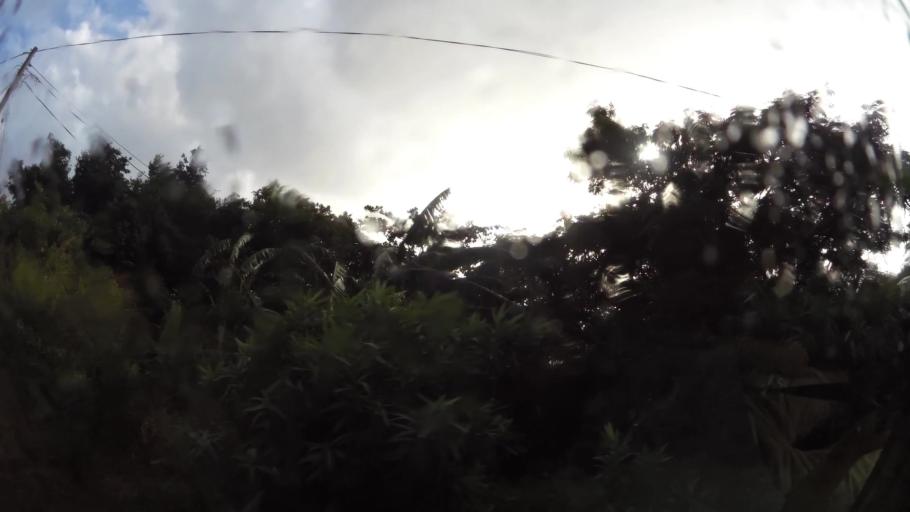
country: DM
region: Saint Paul
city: Mahaut
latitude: 15.3655
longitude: -61.3991
